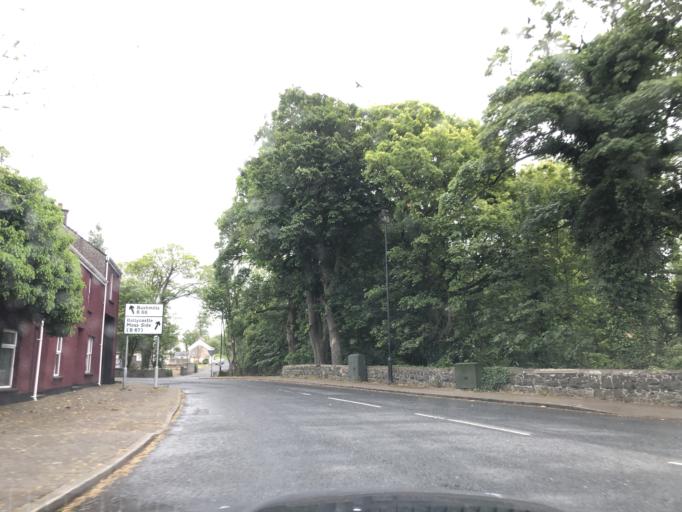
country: GB
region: Northern Ireland
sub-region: Ballymoney District
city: Ballymoney
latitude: 55.1233
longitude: -6.4690
